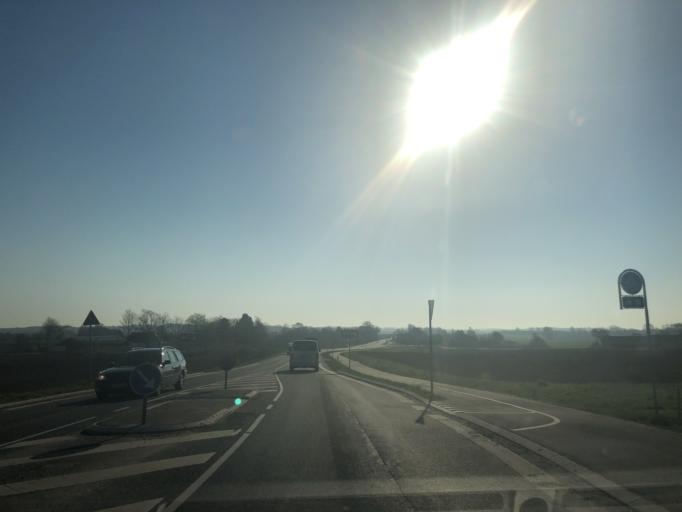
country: DK
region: Zealand
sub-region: Faxe Kommune
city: Ronnede
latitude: 55.2589
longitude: 12.0325
